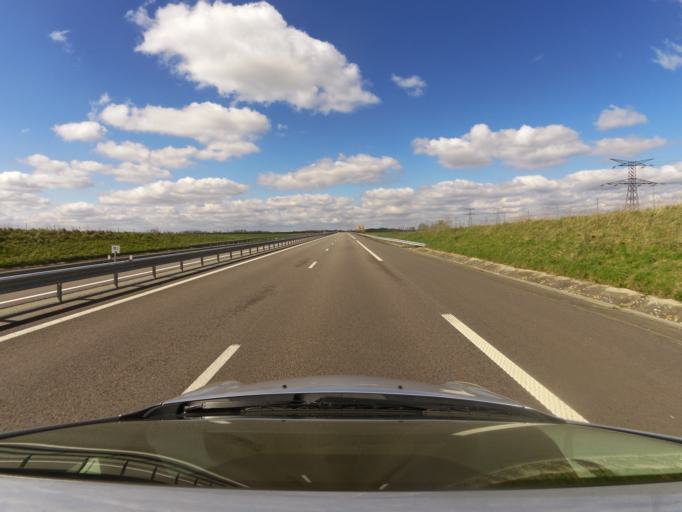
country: FR
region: Haute-Normandie
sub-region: Departement de la Seine-Maritime
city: Cleres
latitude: 49.6347
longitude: 1.1051
